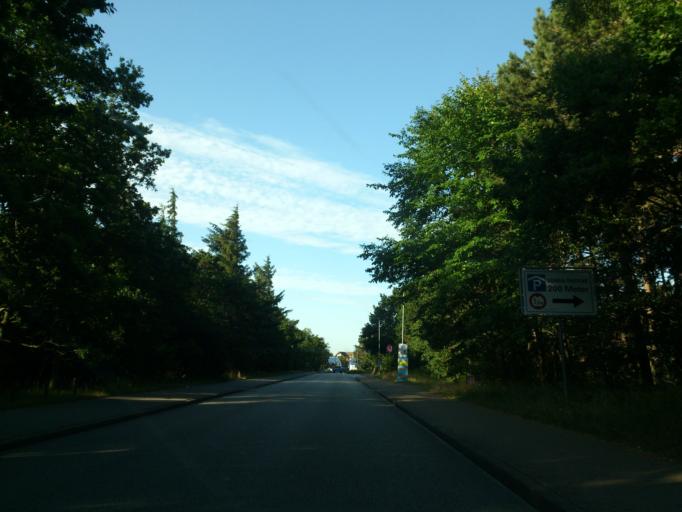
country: DE
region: Schleswig-Holstein
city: Sankt Peter-Ording
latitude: 54.3188
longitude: 8.6098
